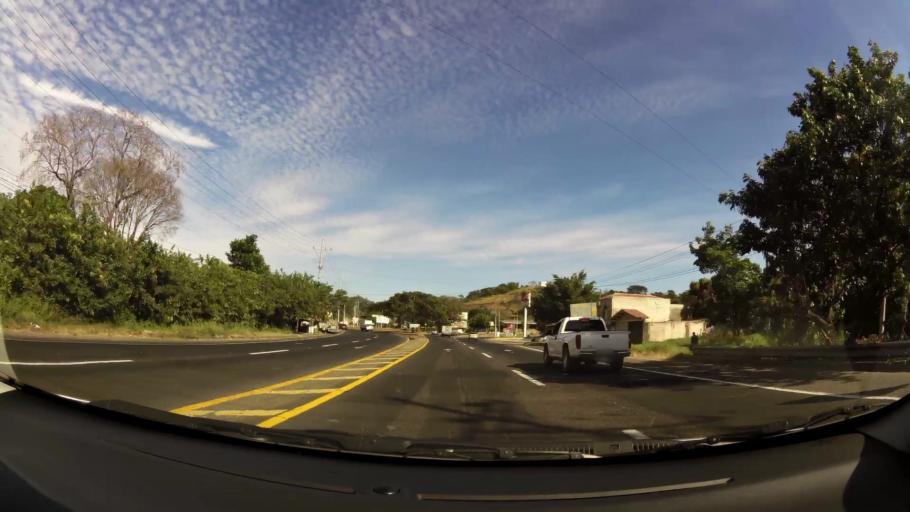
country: SV
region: Santa Ana
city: Santa Ana
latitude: 13.9848
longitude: -89.5982
